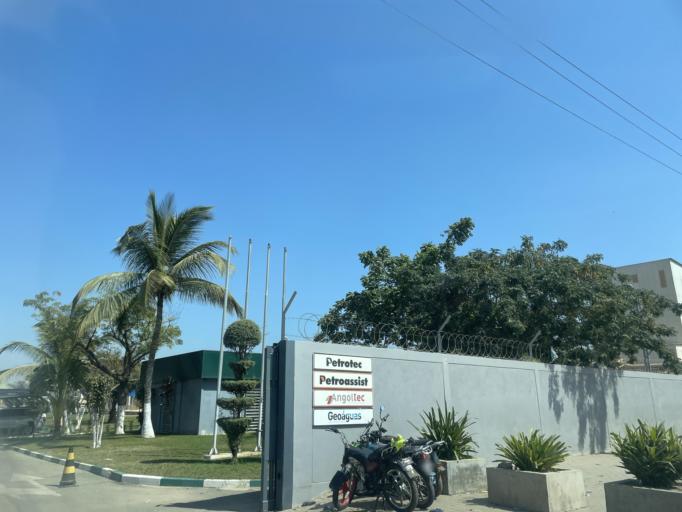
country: AO
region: Luanda
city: Luanda
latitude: -8.7646
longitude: 13.4031
